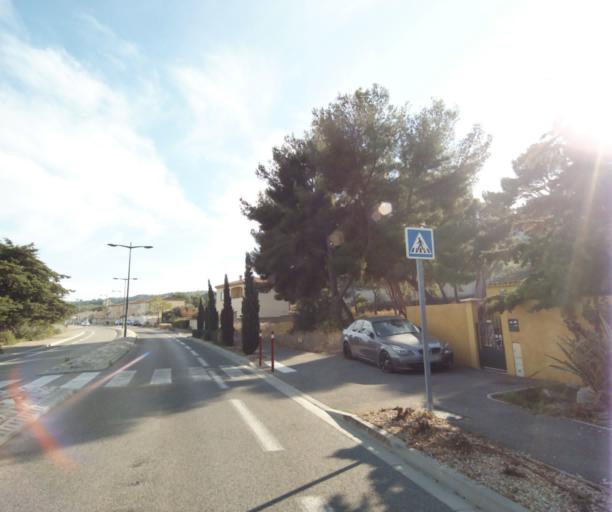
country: FR
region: Provence-Alpes-Cote d'Azur
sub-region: Departement des Bouches-du-Rhone
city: Chateauneuf-les-Martigues
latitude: 43.3761
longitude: 5.1768
